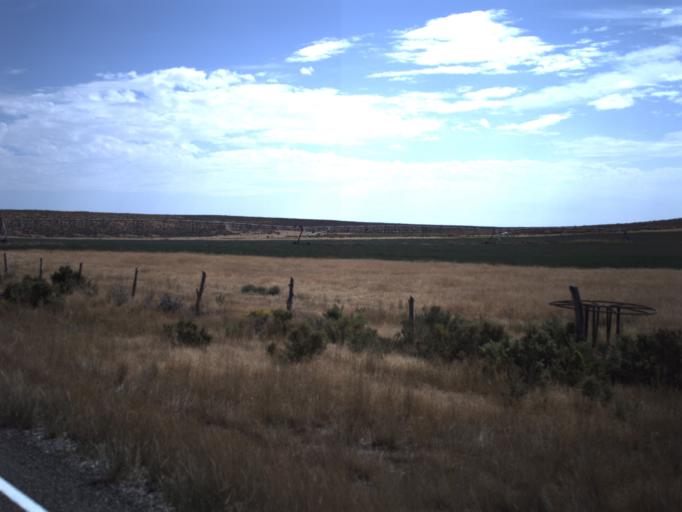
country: US
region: Idaho
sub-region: Cassia County
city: Burley
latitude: 41.8158
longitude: -113.2293
